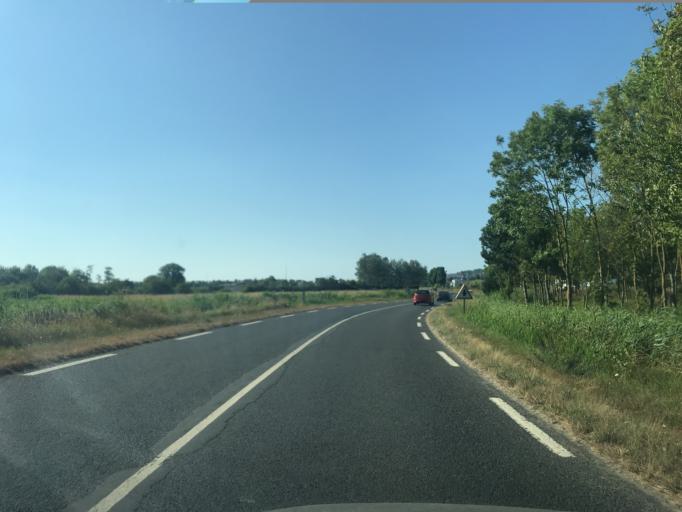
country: FR
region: Lower Normandy
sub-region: Departement du Calvados
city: Touques
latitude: 49.3427
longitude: 0.0952
